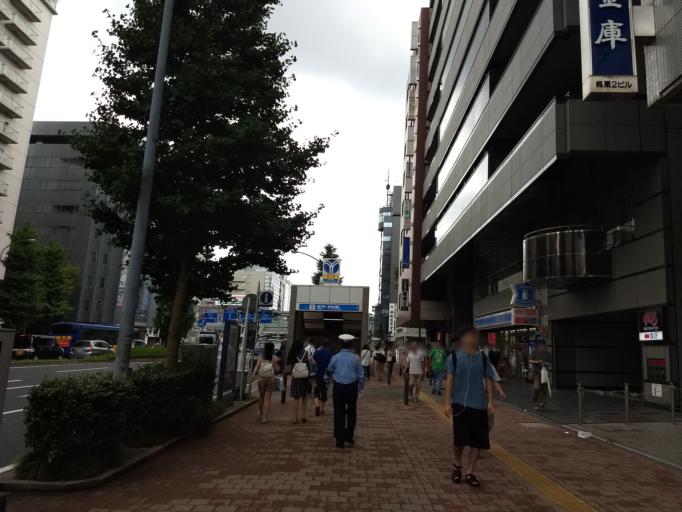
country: JP
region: Kanagawa
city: Yokohama
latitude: 35.5099
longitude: 139.6160
